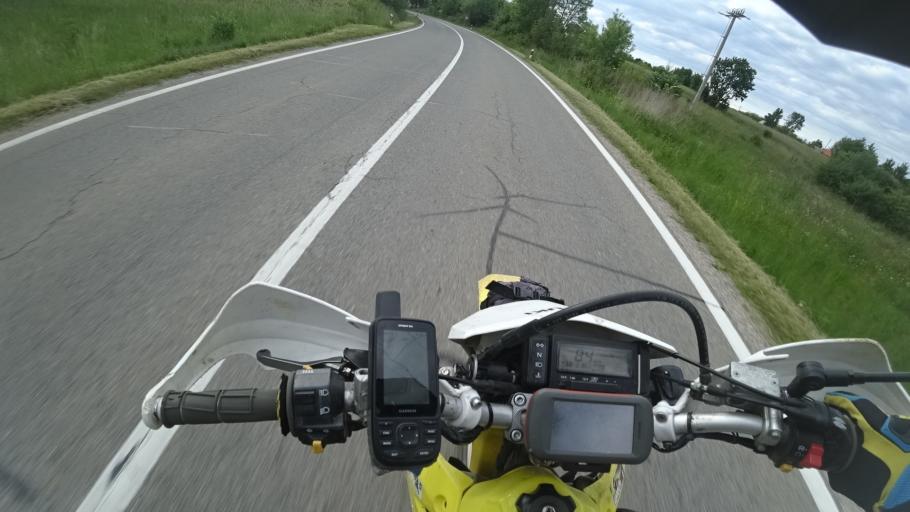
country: HR
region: Licko-Senjska
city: Gospic
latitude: 44.5128
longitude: 15.4260
